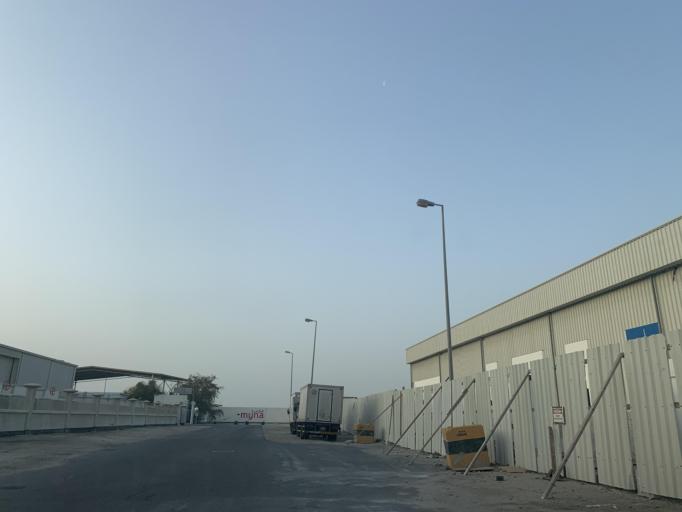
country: BH
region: Manama
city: Manama
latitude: 26.1962
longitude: 50.5939
